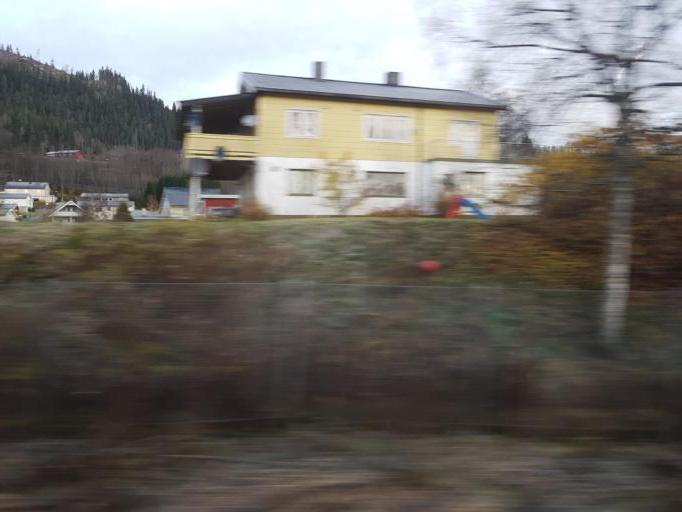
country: NO
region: Sor-Trondelag
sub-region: Midtre Gauldal
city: Storen
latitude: 63.0327
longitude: 10.2781
